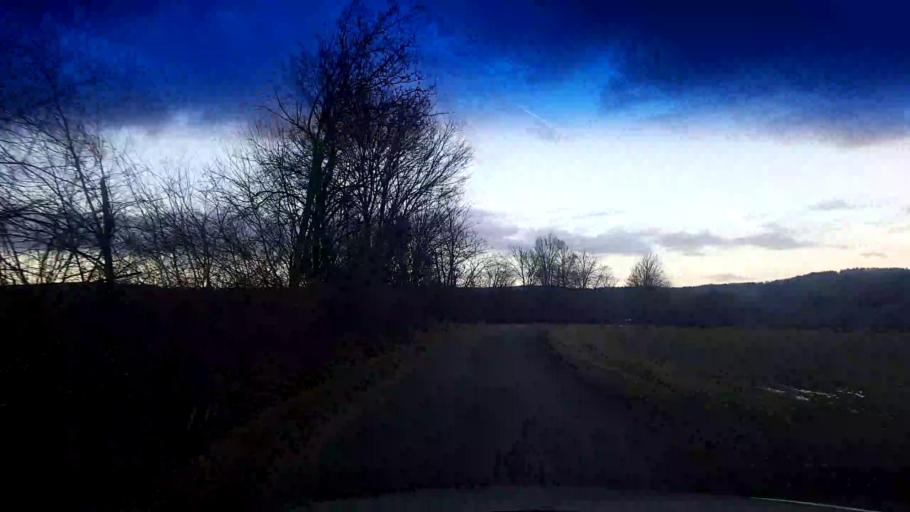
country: DE
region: Bavaria
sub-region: Upper Franconia
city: Buttenheim
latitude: 49.8132
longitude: 11.0531
